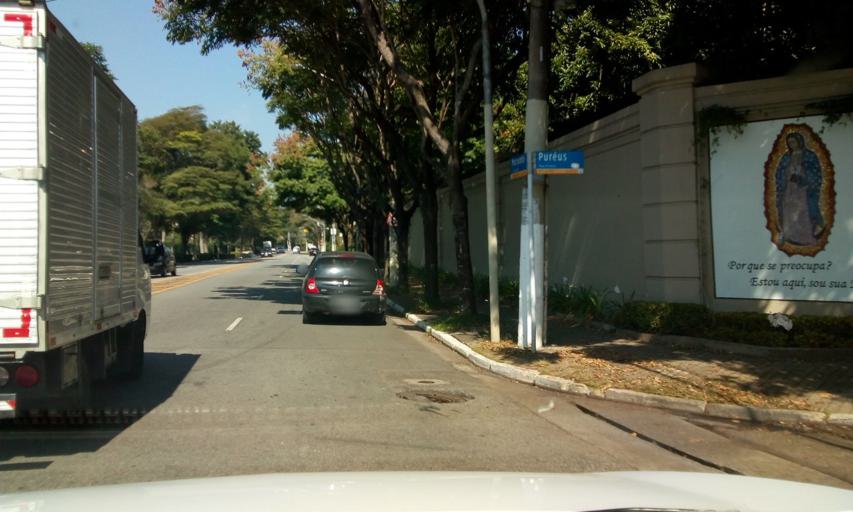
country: BR
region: Sao Paulo
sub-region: Sao Paulo
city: Sao Paulo
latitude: -23.5871
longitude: -46.7060
